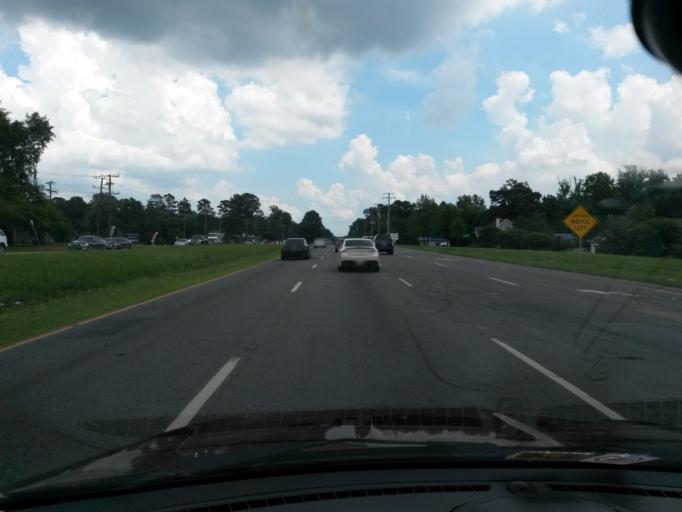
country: US
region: Virginia
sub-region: Chesterfield County
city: Enon
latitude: 37.3483
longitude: -77.3553
